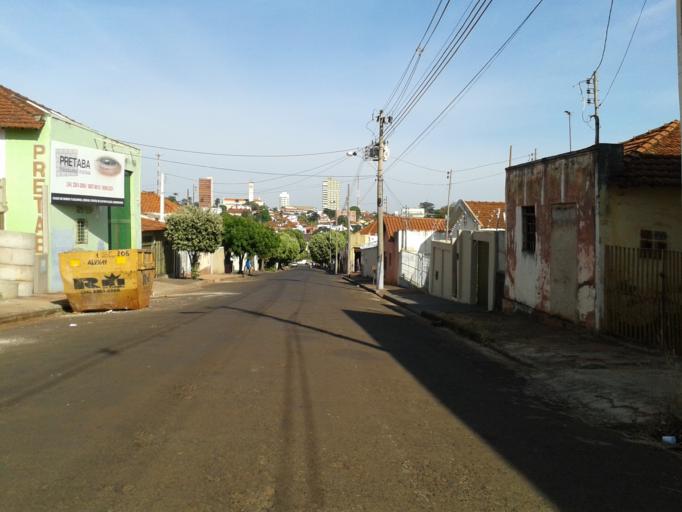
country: BR
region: Minas Gerais
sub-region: Ituiutaba
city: Ituiutaba
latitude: -18.9668
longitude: -49.4570
